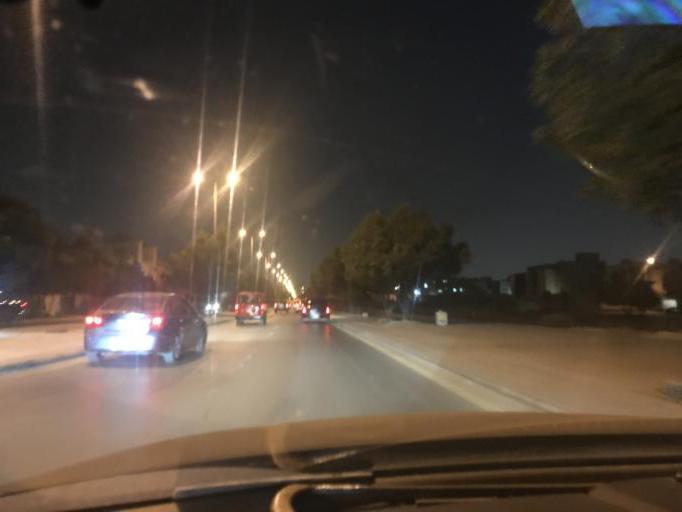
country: SA
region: Ar Riyad
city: Riyadh
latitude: 24.6815
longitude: 46.7951
